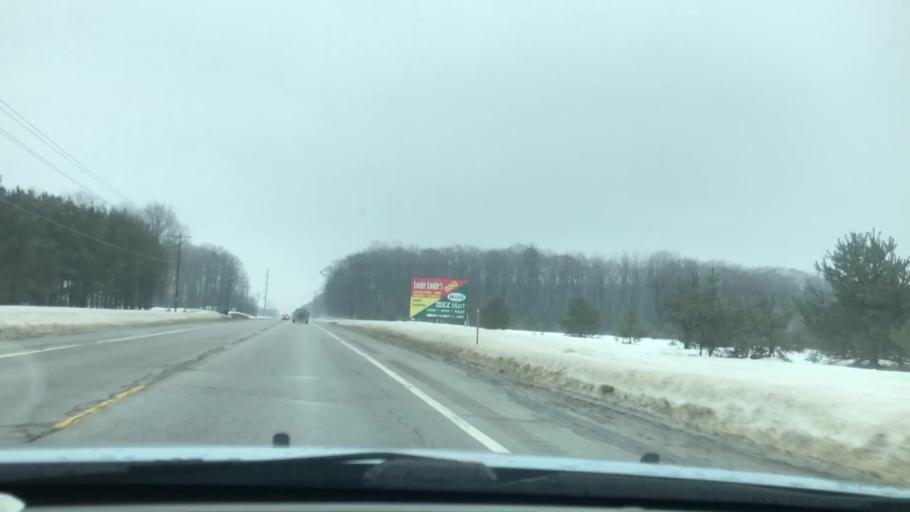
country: US
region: Michigan
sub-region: Otsego County
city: Gaylord
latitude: 45.0278
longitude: -84.7600
